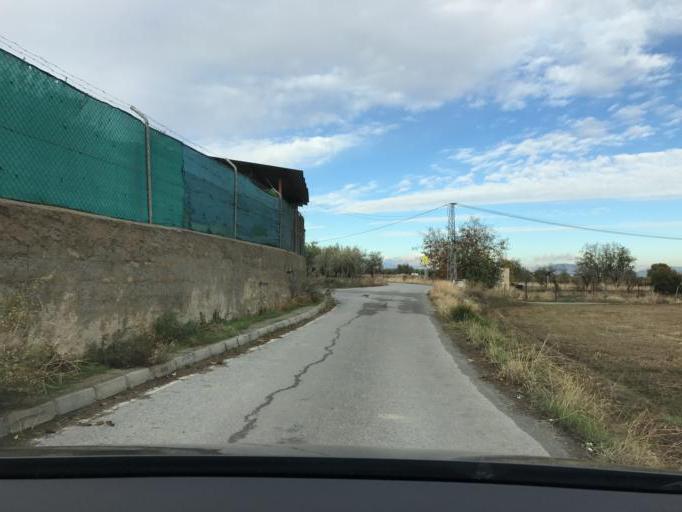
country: ES
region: Andalusia
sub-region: Provincia de Granada
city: Ogijares
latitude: 37.1220
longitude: -3.5976
